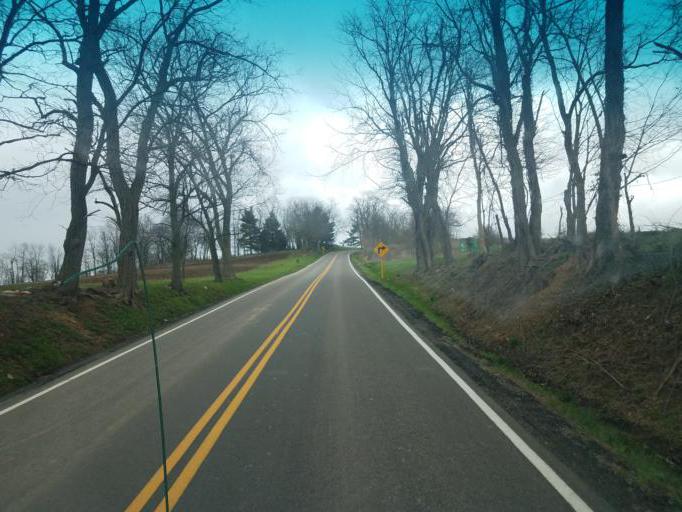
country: US
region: Ohio
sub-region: Stark County
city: Beach City
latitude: 40.6175
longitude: -81.7030
